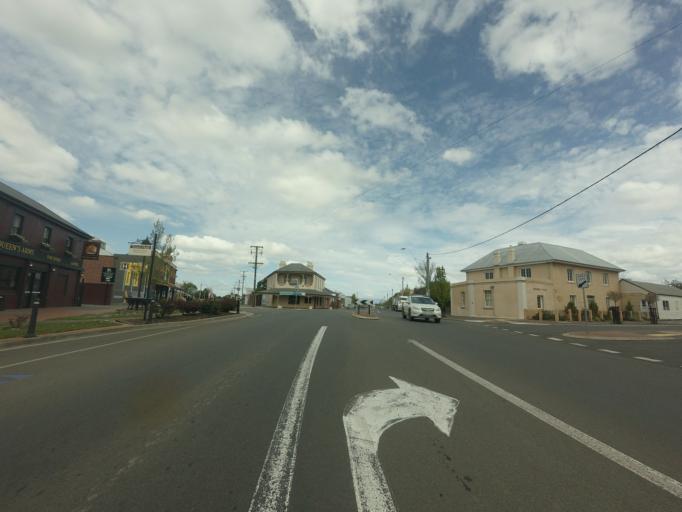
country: AU
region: Tasmania
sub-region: Northern Midlands
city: Longford
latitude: -41.5946
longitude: 147.1222
